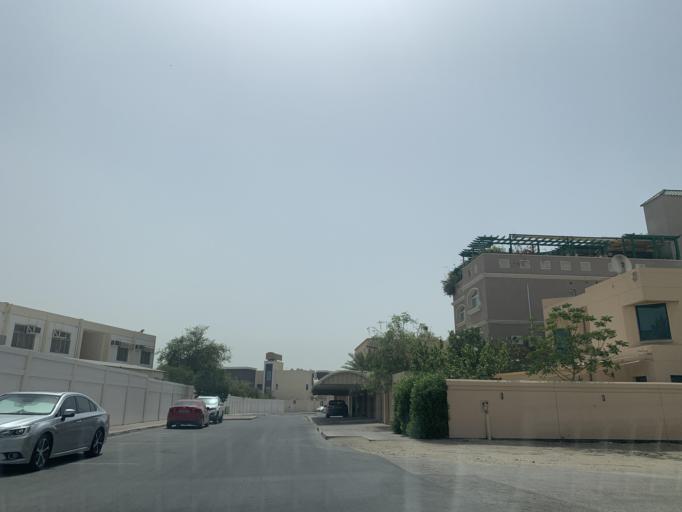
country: BH
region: Northern
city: Madinat `Isa
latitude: 26.1535
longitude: 50.5243
